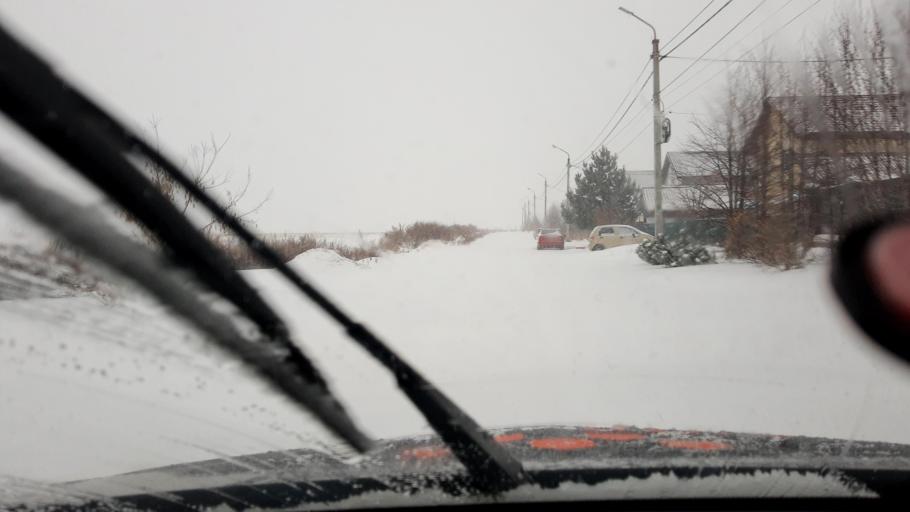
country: RU
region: Bashkortostan
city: Ufa
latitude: 54.8569
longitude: 56.0134
